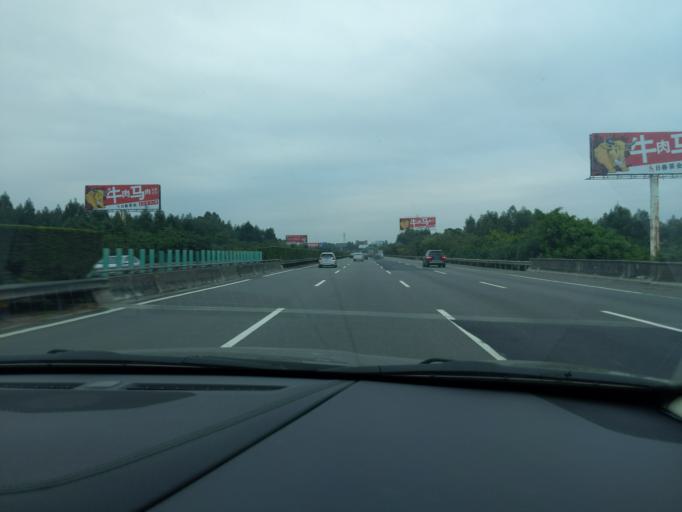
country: CN
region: Fujian
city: Neikeng
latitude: 24.7651
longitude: 118.4504
